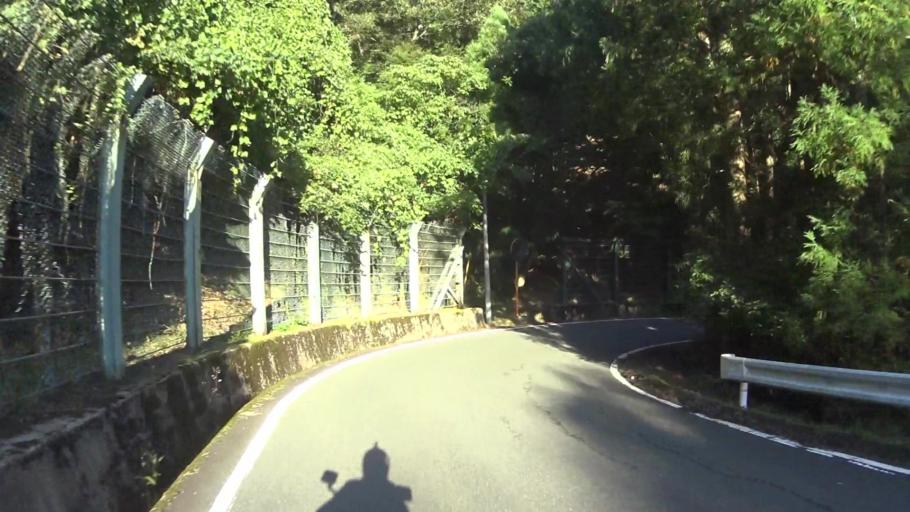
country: JP
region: Hyogo
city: Toyooka
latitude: 35.6130
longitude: 134.8801
